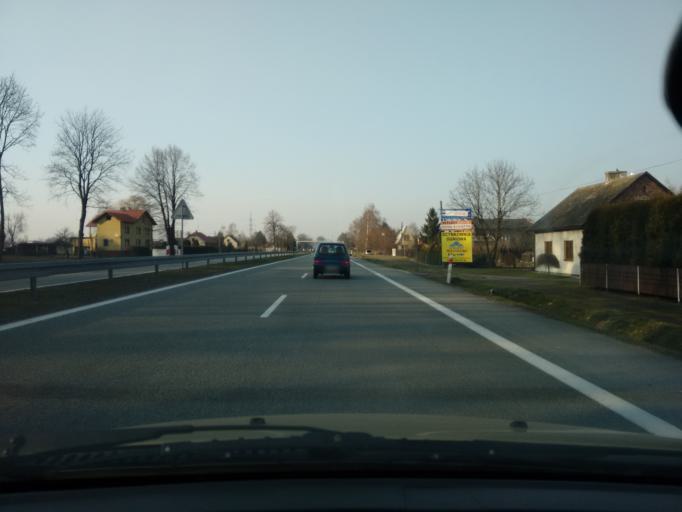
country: PL
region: Silesian Voivodeship
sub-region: Powiat cieszynski
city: Zbytkow
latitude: 49.9126
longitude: 18.7355
